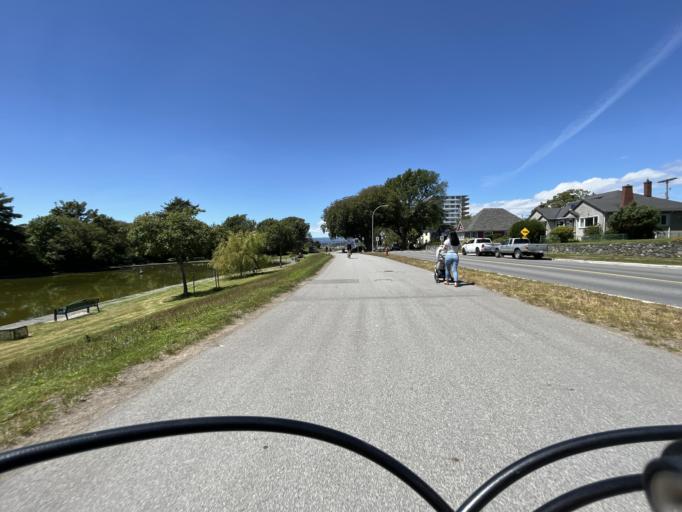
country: CA
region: British Columbia
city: Victoria
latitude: 48.4099
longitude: -123.3734
